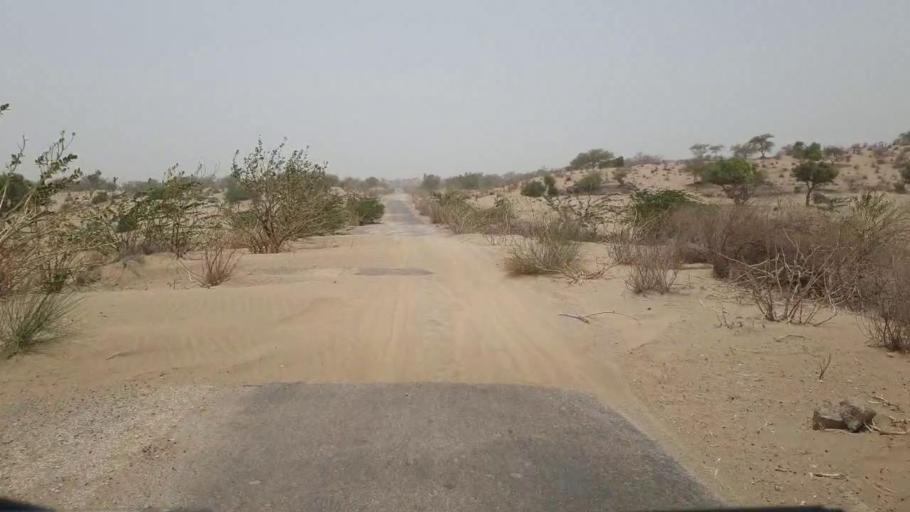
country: PK
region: Sindh
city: Naukot
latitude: 24.7642
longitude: 69.5436
